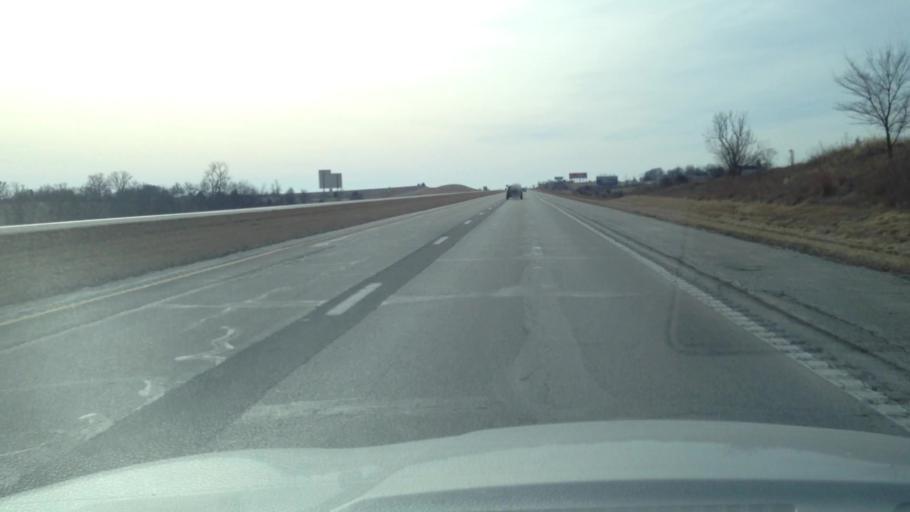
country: US
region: Missouri
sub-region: Harrison County
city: Bethany
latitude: 40.3569
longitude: -94.0080
